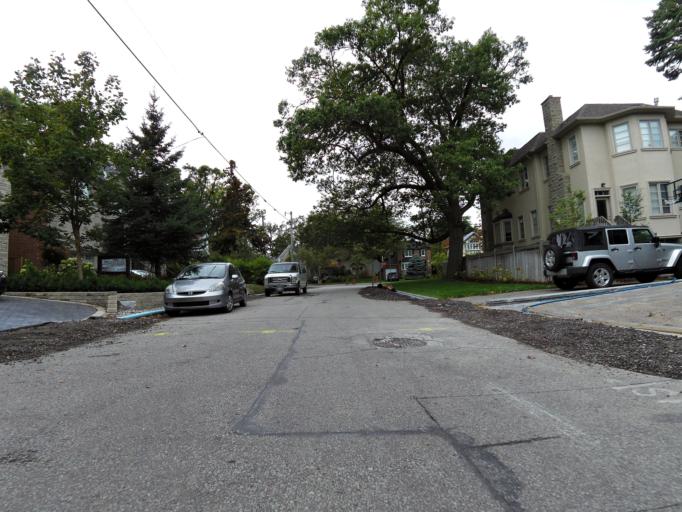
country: CA
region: Ontario
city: Scarborough
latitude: 43.6811
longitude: -79.2781
